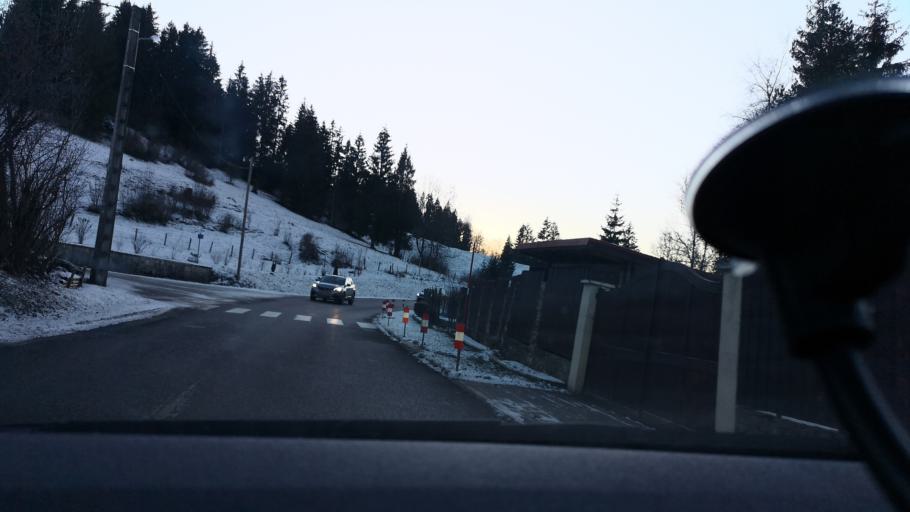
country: FR
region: Franche-Comte
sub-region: Departement du Doubs
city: Pontarlier
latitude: 46.8515
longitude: 6.3285
